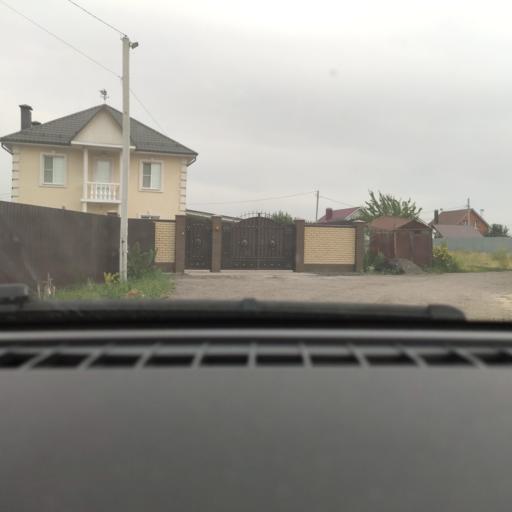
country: RU
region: Voronezj
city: Novaya Usman'
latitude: 51.6466
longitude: 39.3398
